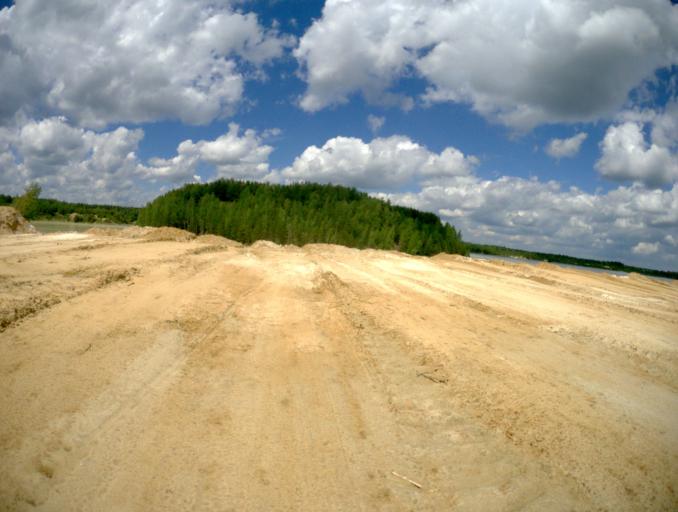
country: RU
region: Vladimir
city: Velikodvorskiy
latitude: 55.2275
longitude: 40.6396
